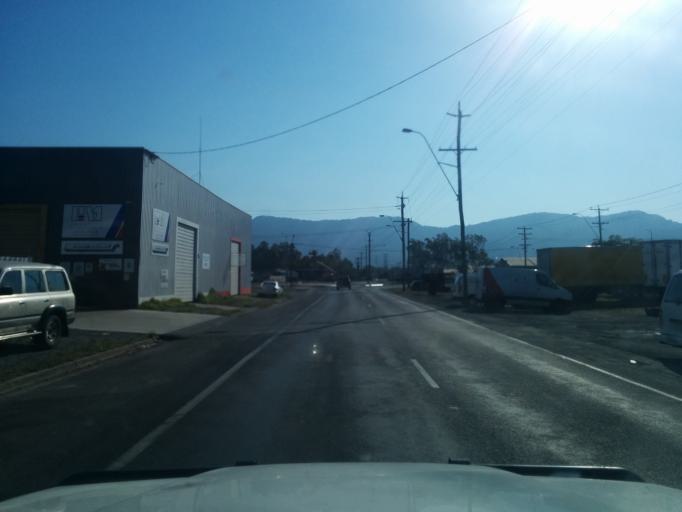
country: AU
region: Queensland
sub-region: Cairns
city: Woree
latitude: -16.9415
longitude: 145.7593
